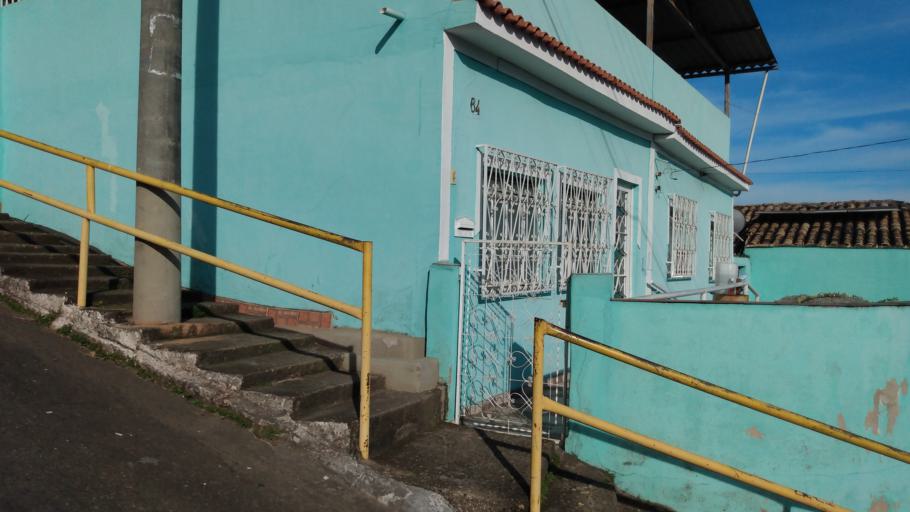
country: BR
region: Minas Gerais
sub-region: Sao Joao Del Rei
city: Sao Joao del Rei
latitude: -21.1428
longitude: -44.2571
